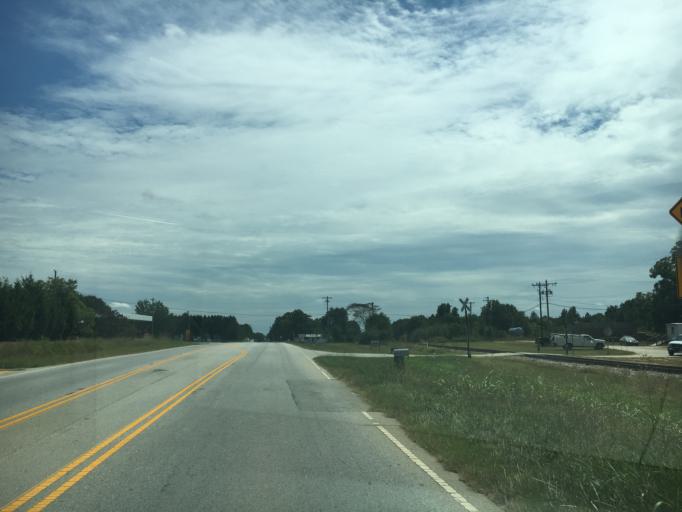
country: US
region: South Carolina
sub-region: Laurens County
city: Laurens
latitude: 34.5714
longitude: -82.0885
